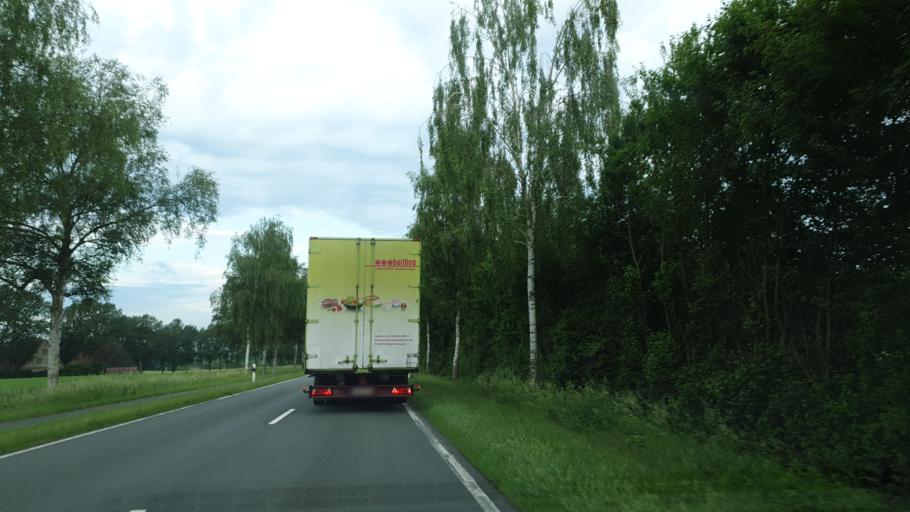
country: DE
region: North Rhine-Westphalia
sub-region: Regierungsbezirk Munster
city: Telgte
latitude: 52.0257
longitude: 7.7965
